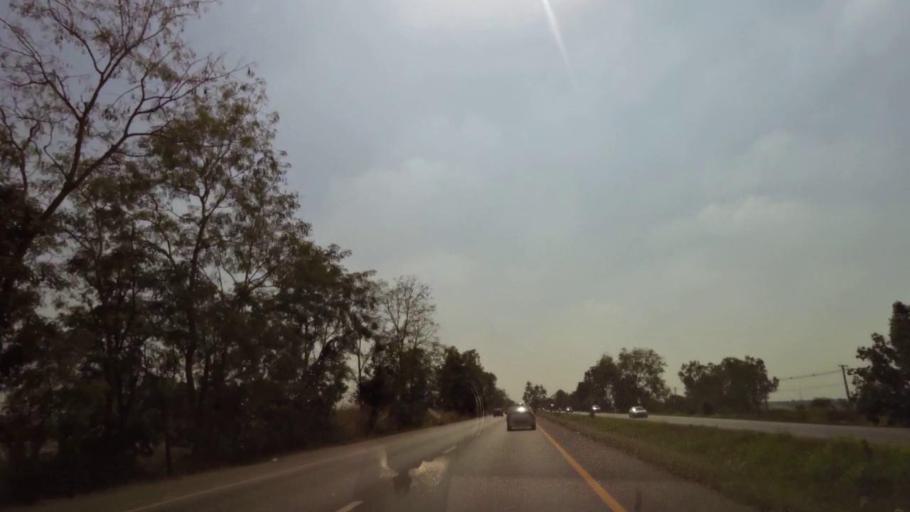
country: TH
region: Phichit
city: Wachira Barami
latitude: 16.4538
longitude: 100.1467
